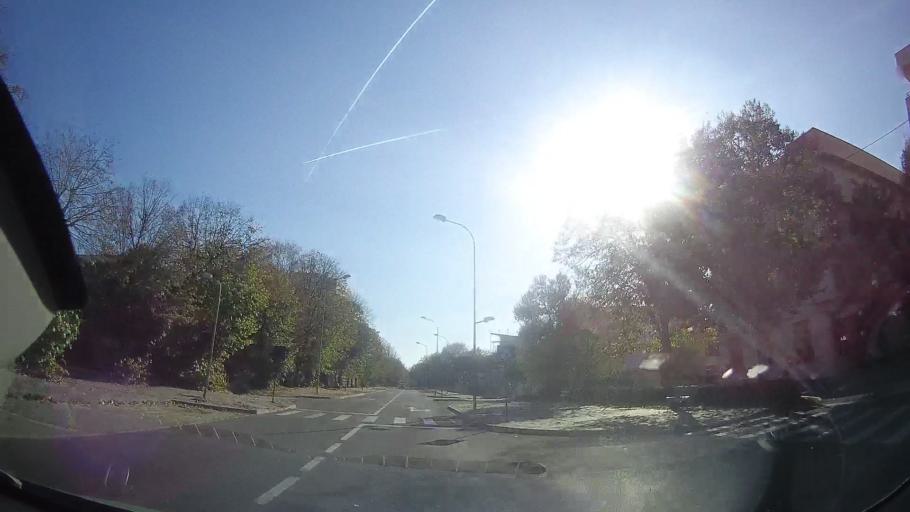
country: RO
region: Constanta
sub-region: Comuna Douazeci si Trei August
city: Douazeci si Trei August
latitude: 43.8797
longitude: 28.6031
